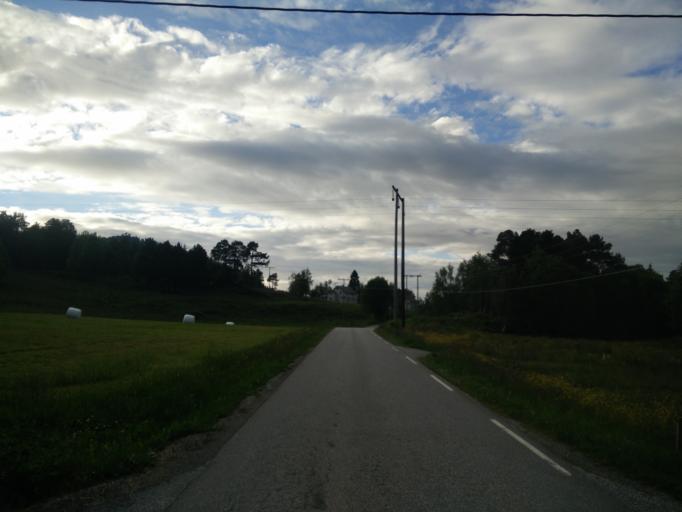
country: NO
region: More og Romsdal
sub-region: Kristiansund
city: Rensvik
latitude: 63.0167
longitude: 7.9636
